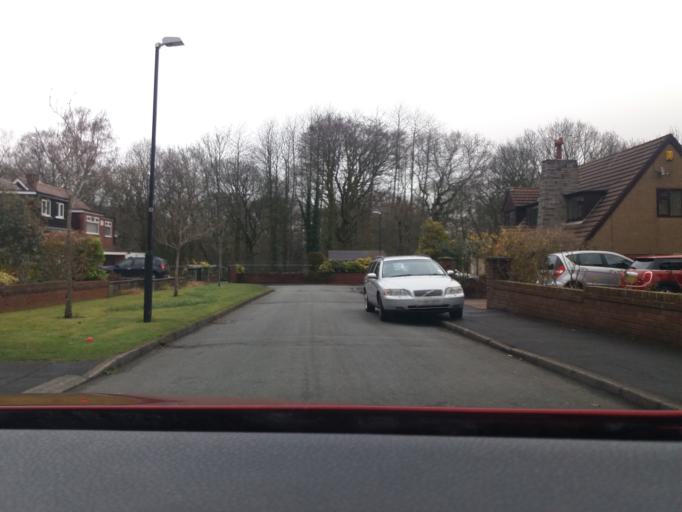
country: GB
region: England
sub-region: Lancashire
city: Chorley
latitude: 53.6557
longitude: -2.6414
